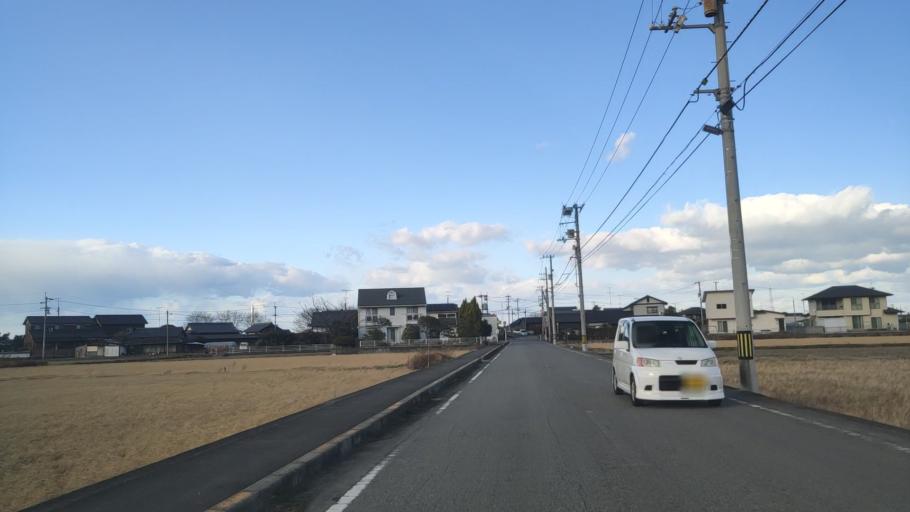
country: JP
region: Ehime
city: Saijo
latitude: 33.9050
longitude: 133.1292
